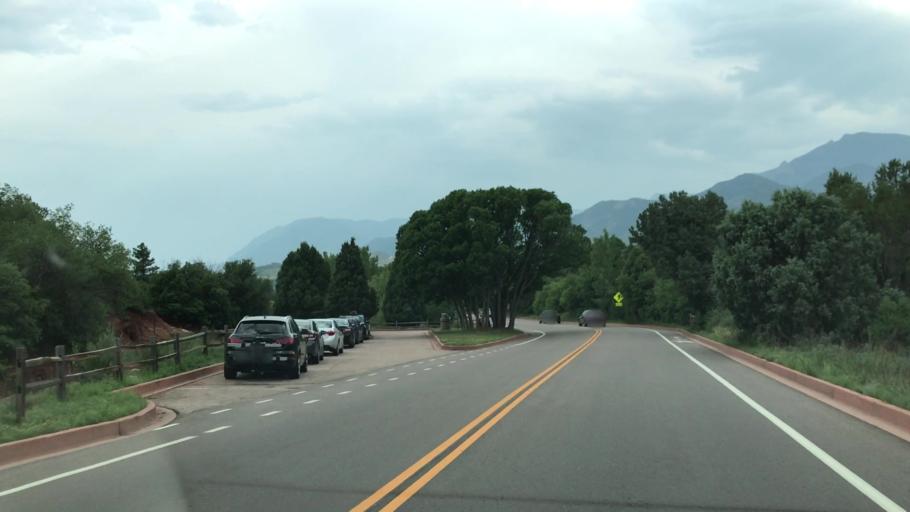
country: US
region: Colorado
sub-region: El Paso County
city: Manitou Springs
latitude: 38.8736
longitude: -104.8852
